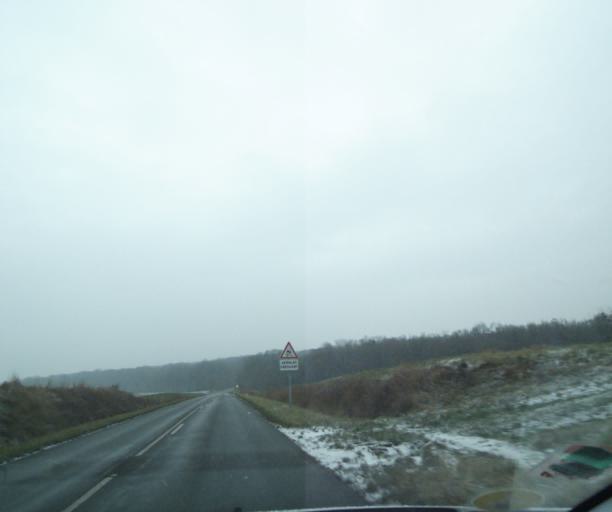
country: FR
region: Champagne-Ardenne
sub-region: Departement de la Haute-Marne
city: Wassy
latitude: 48.4784
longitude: 5.0087
